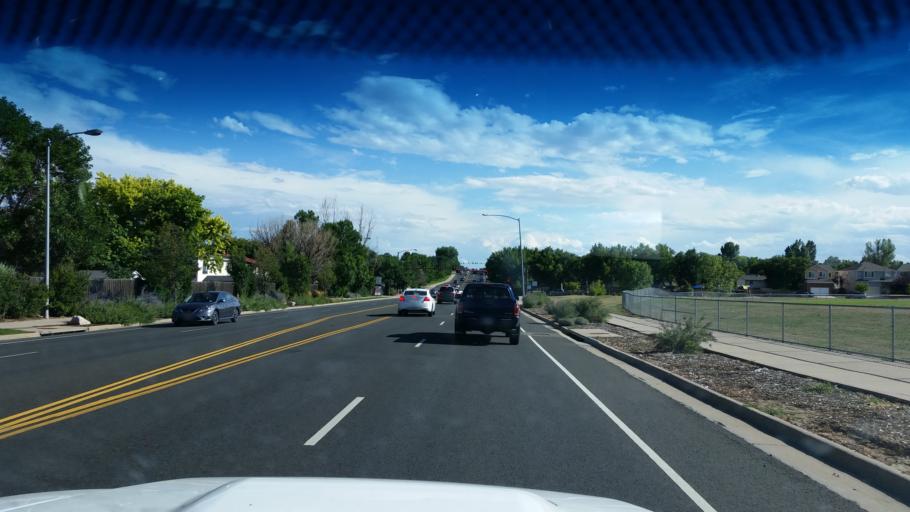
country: US
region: Colorado
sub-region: Adams County
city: Northglenn
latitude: 39.9229
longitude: -104.9404
